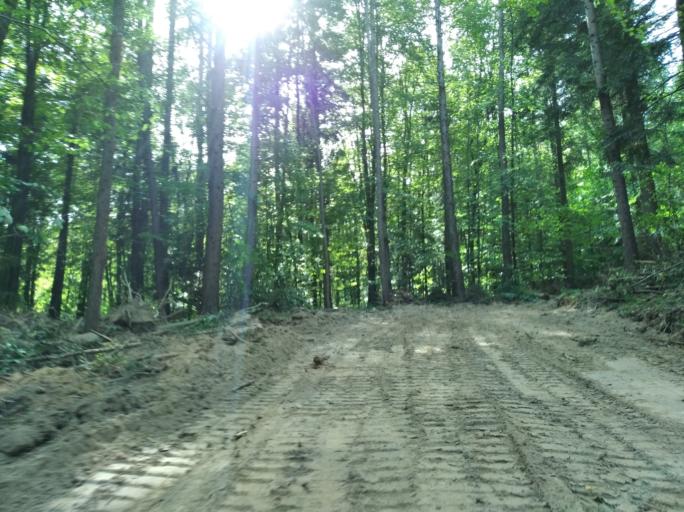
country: PL
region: Subcarpathian Voivodeship
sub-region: Powiat strzyzowski
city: Wisniowa
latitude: 49.8791
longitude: 21.6289
